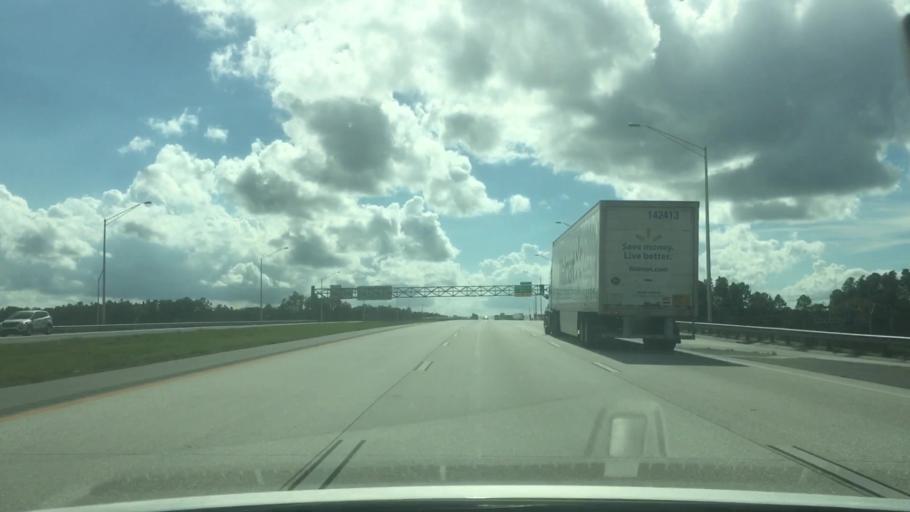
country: US
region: Florida
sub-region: Saint Johns County
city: Palm Valley
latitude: 30.1372
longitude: -81.5090
